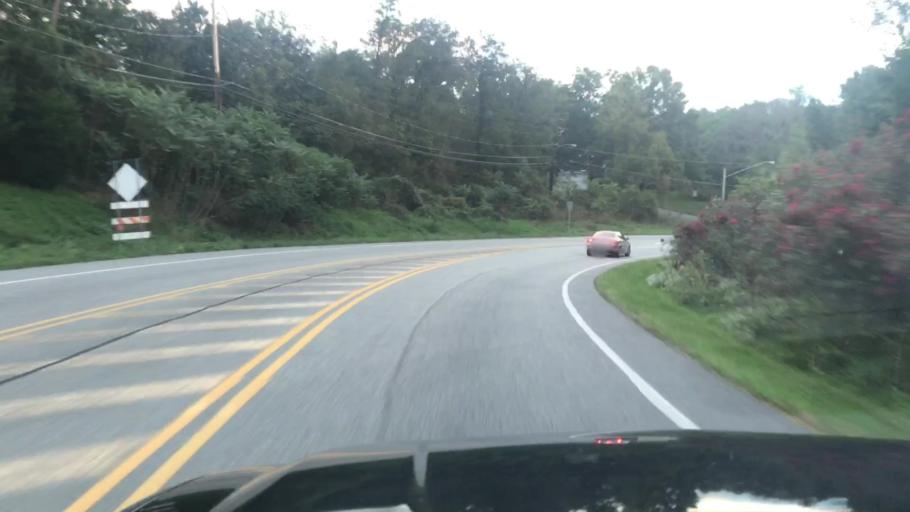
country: US
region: Pennsylvania
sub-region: Cumberland County
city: Mechanicsburg
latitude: 40.2636
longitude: -76.9894
